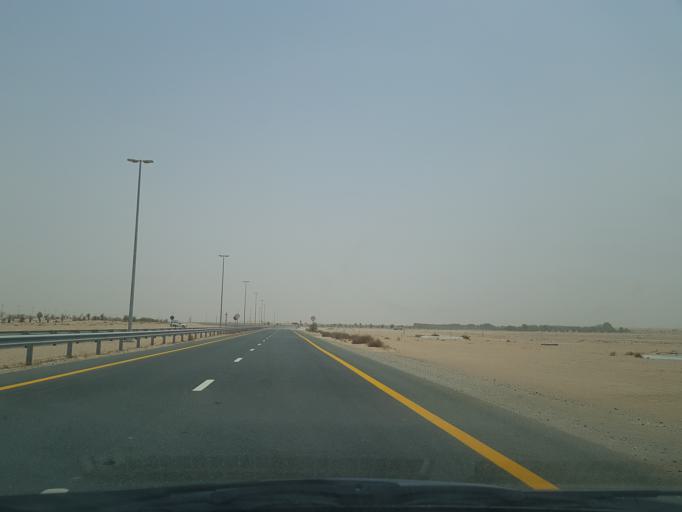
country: AE
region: Dubai
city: Dubai
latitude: 24.8741
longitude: 55.4177
